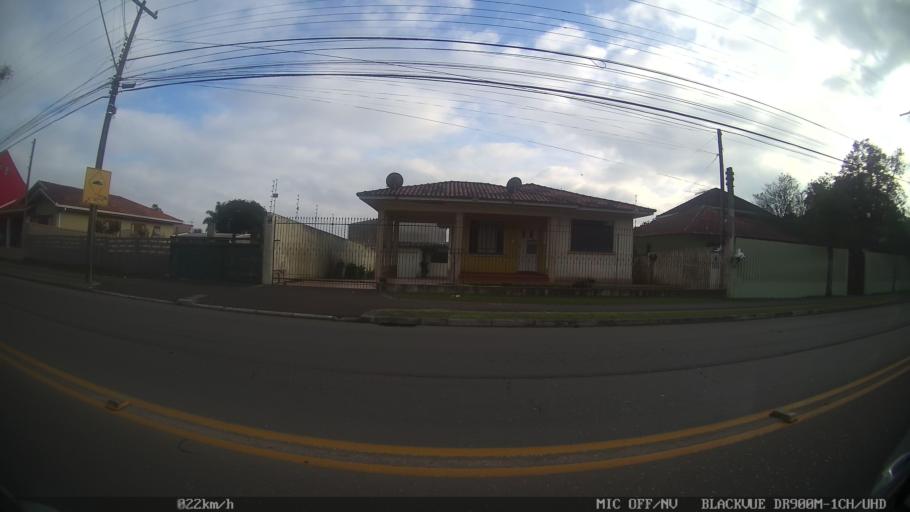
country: BR
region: Parana
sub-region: Almirante Tamandare
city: Almirante Tamandare
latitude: -25.3943
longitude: -49.3447
